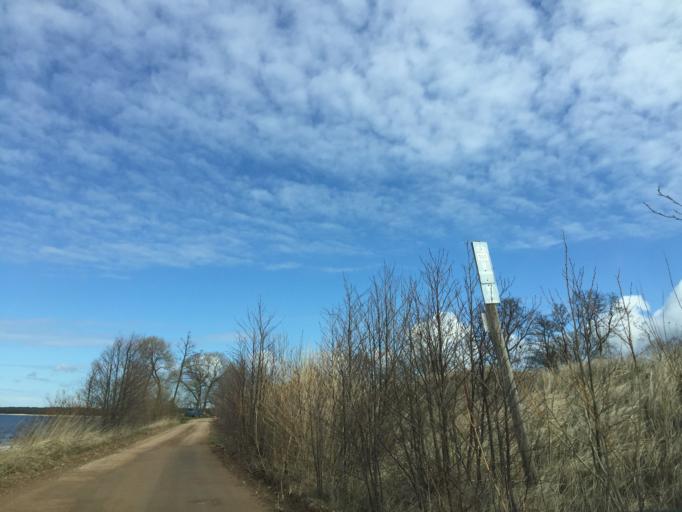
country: LV
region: Salacgrivas
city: Salacgriva
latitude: 57.6055
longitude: 24.3789
